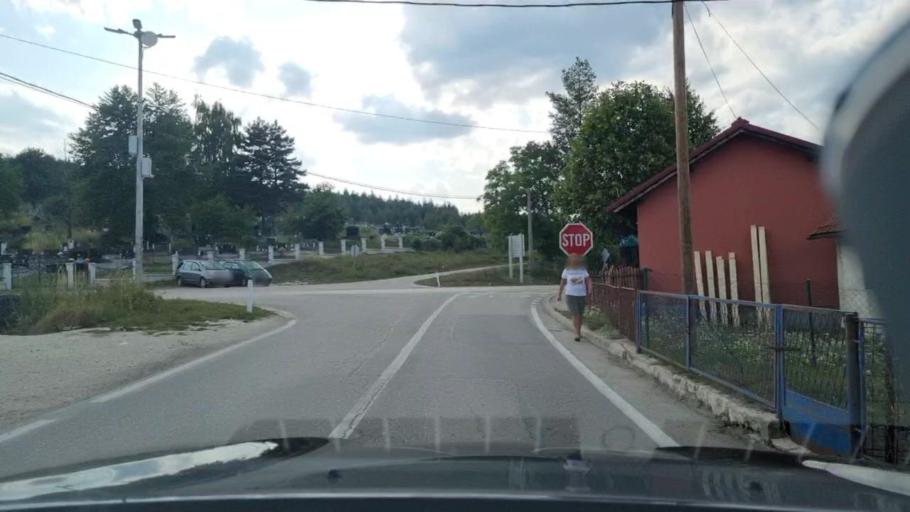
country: BA
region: Federation of Bosnia and Herzegovina
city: Glamoc
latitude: 44.0488
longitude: 16.8438
